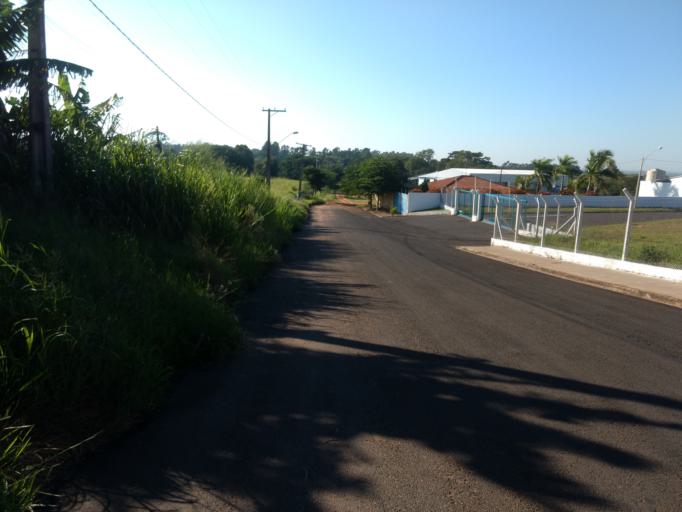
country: BR
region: Sao Paulo
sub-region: Junqueiropolis
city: Junqueiropolis
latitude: -21.4958
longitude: -51.5306
